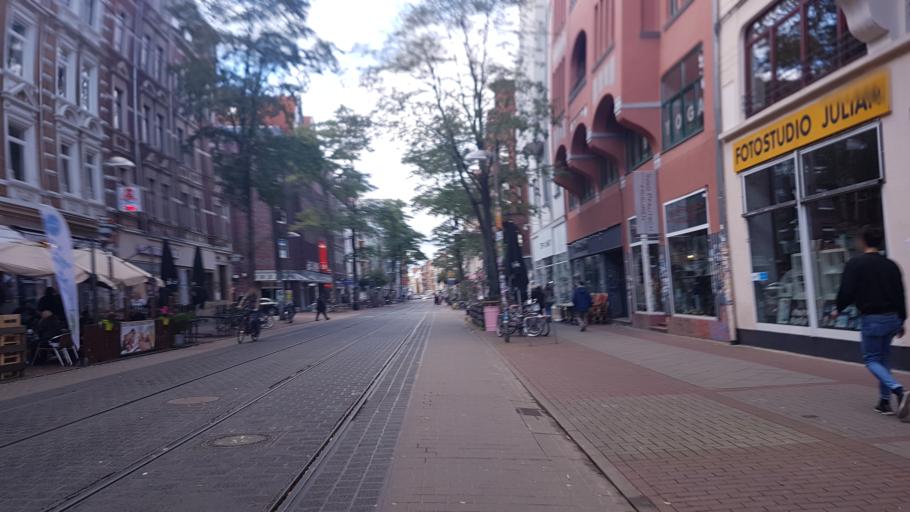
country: DE
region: Lower Saxony
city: Hannover
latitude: 52.3734
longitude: 9.7079
